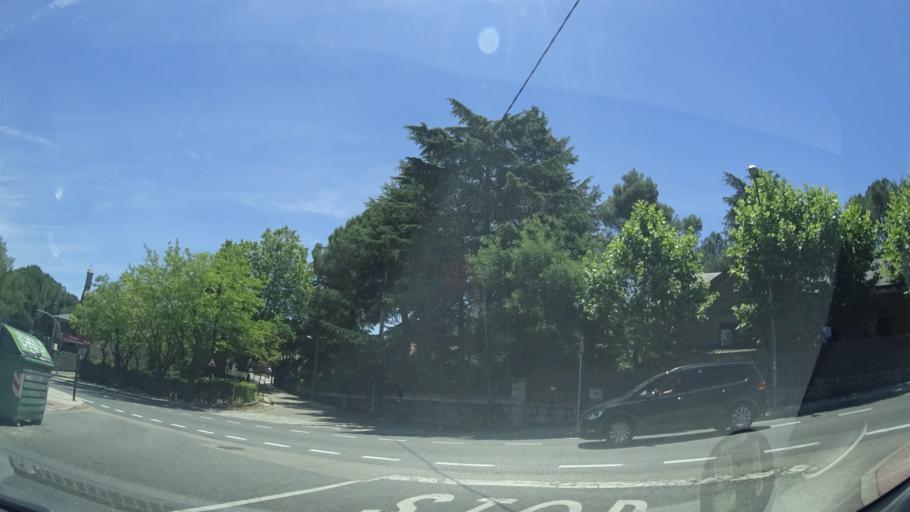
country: ES
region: Madrid
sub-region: Provincia de Madrid
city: Galapagar
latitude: 40.5945
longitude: -3.9866
